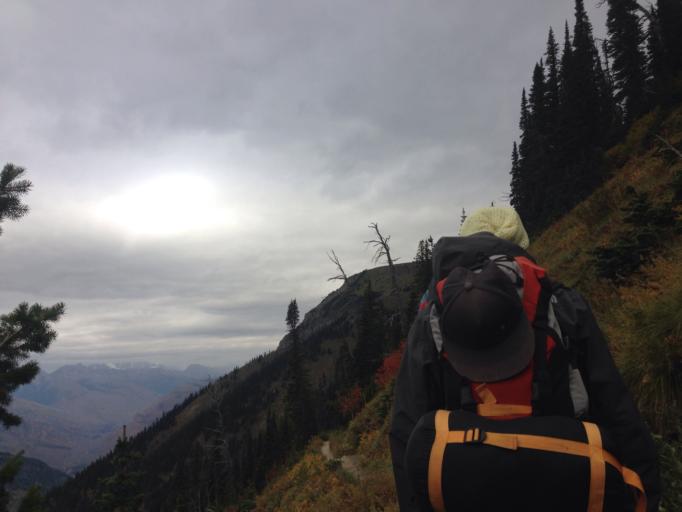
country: US
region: Montana
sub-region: Flathead County
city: Columbia Falls
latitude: 48.7205
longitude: -113.7196
